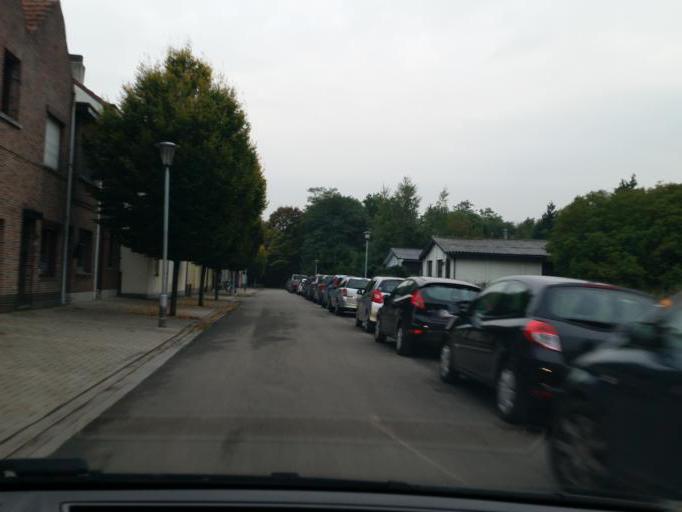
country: BE
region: Flanders
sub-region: Provincie Antwerpen
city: Hemiksem
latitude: 51.1392
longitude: 4.3357
